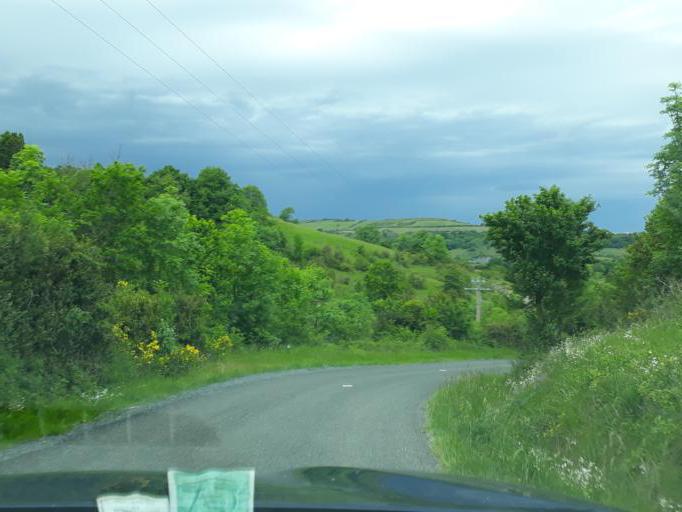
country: FR
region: Languedoc-Roussillon
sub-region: Departement de l'Herault
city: Lodeve
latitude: 43.8164
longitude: 3.2687
